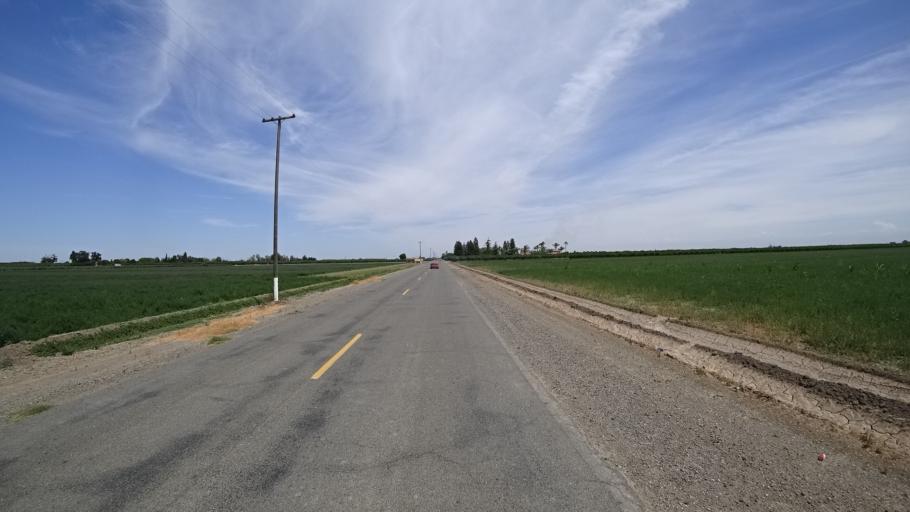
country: US
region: California
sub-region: Kings County
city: Lucerne
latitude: 36.3827
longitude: -119.6910
